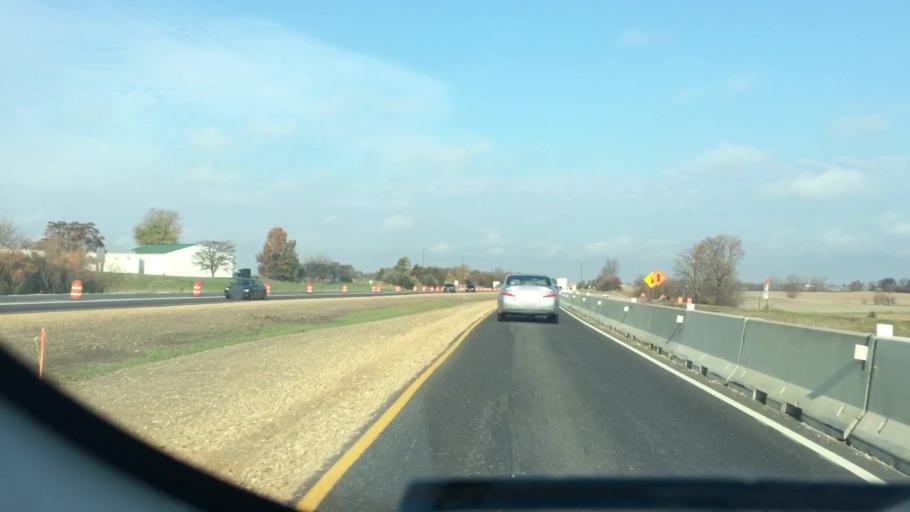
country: US
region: Illinois
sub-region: McLean County
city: Danvers
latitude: 40.5826
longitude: -89.1420
